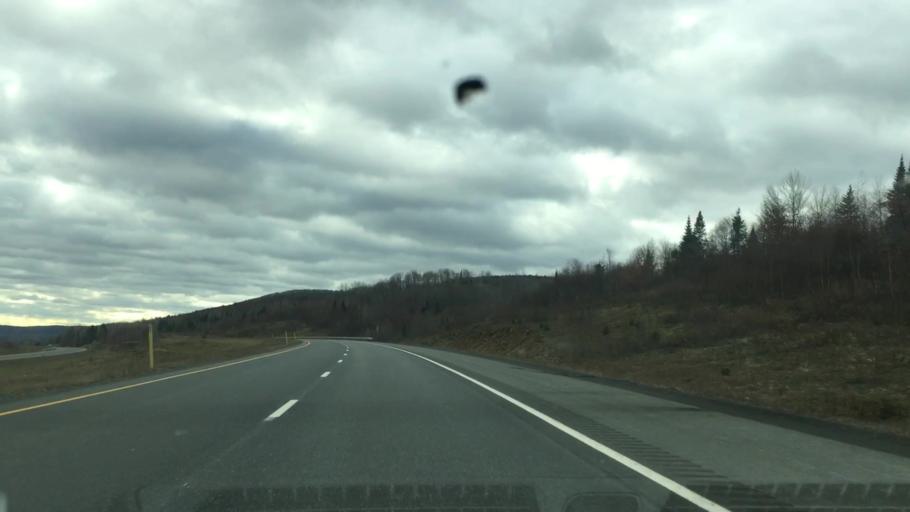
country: US
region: Maine
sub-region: Aroostook County
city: Fort Fairfield
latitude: 46.6988
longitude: -67.7408
